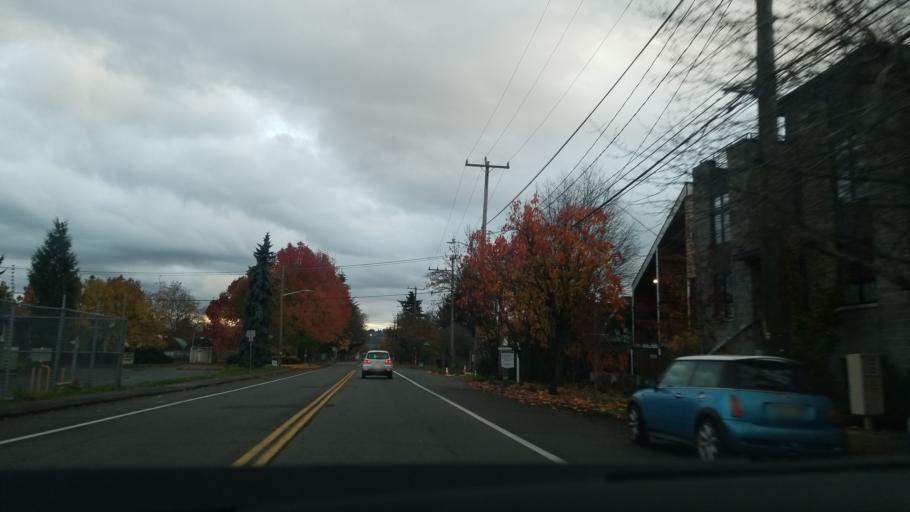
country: US
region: Washington
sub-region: King County
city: White Center
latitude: 47.5448
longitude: -122.3185
